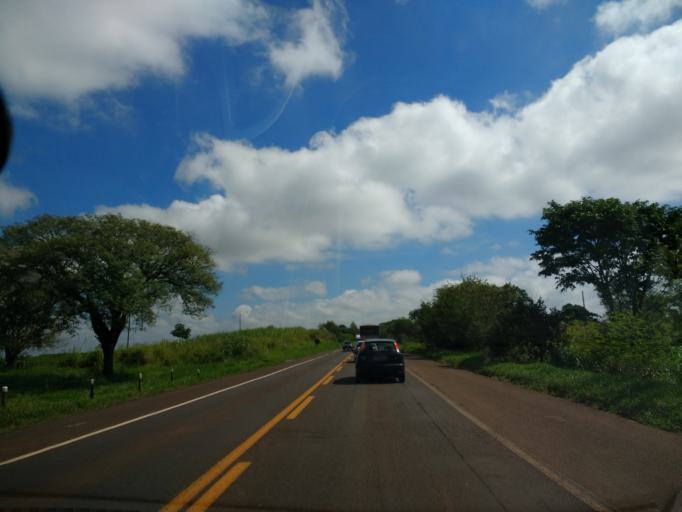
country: BR
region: Parana
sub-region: Cruzeiro Do Oeste
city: Cruzeiro do Oeste
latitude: -23.7711
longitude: -53.1692
